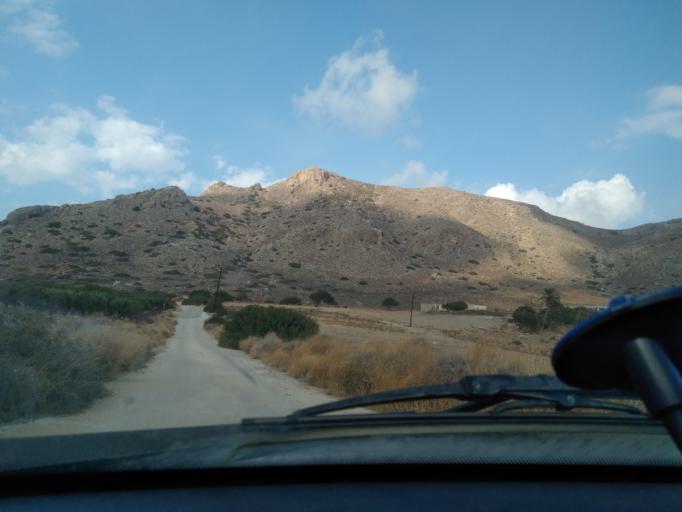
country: GR
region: Crete
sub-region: Nomos Lasithiou
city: Makry-Gialos
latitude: 35.0267
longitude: 26.0129
